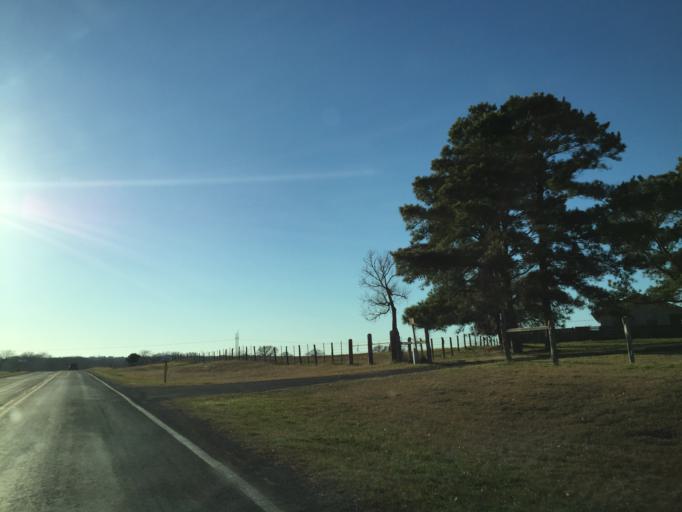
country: US
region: Texas
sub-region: Bastrop County
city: Elgin
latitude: 30.3599
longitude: -97.3438
